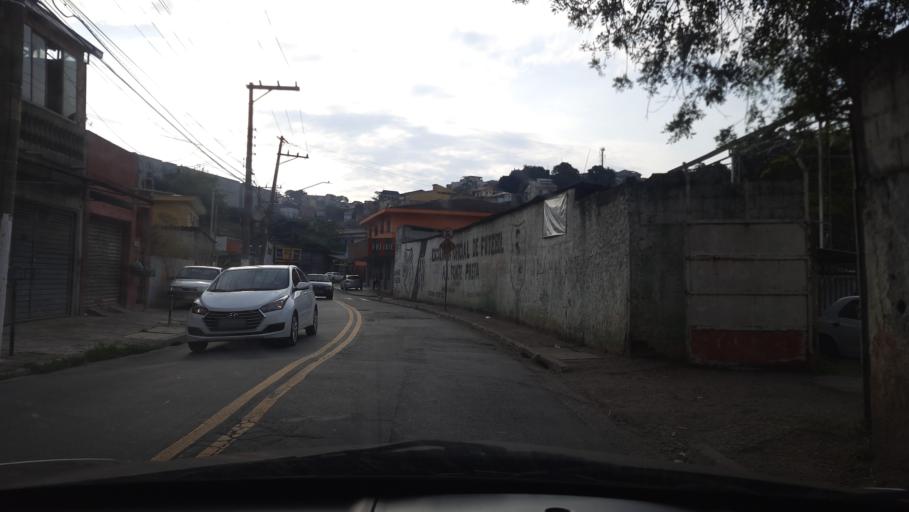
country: BR
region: Sao Paulo
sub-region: Caieiras
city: Caieiras
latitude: -23.4477
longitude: -46.7428
